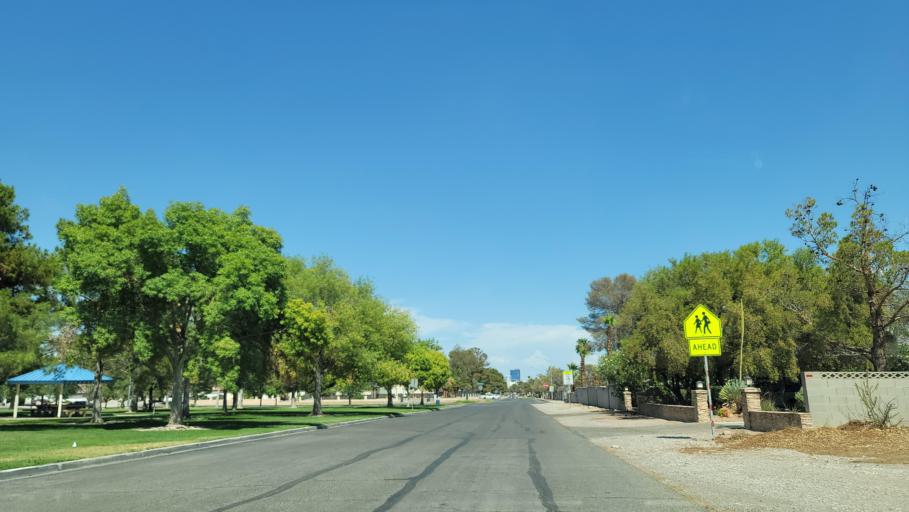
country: US
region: Nevada
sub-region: Clark County
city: Spring Valley
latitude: 36.1386
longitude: -115.2376
